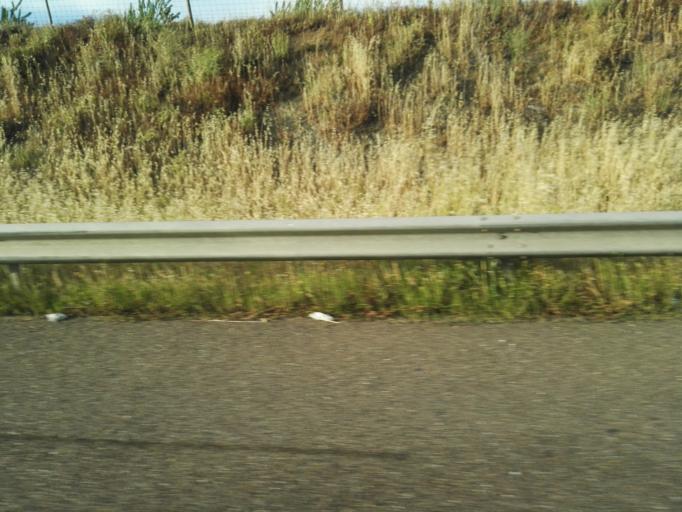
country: PT
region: Portalegre
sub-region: Elvas
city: Elvas
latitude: 38.8926
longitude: -7.1173
